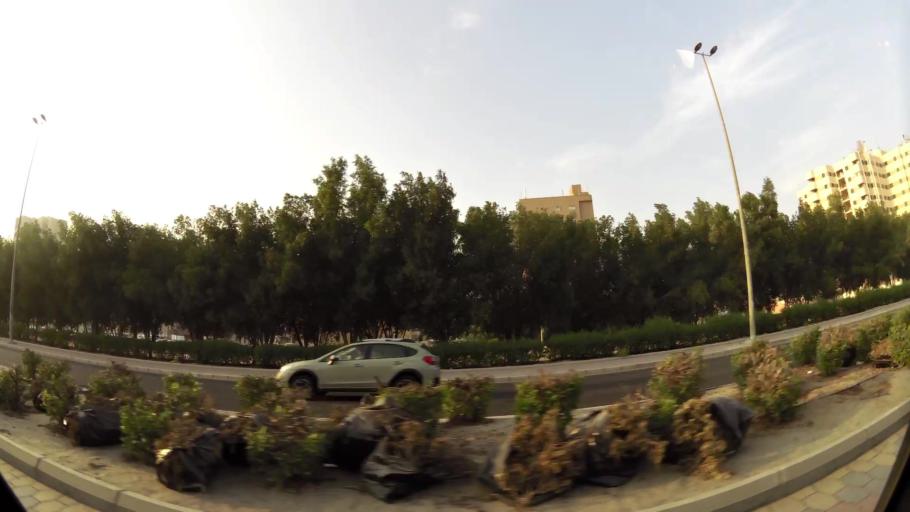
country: KW
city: Al Funaytis
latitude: 29.2474
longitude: 48.0860
